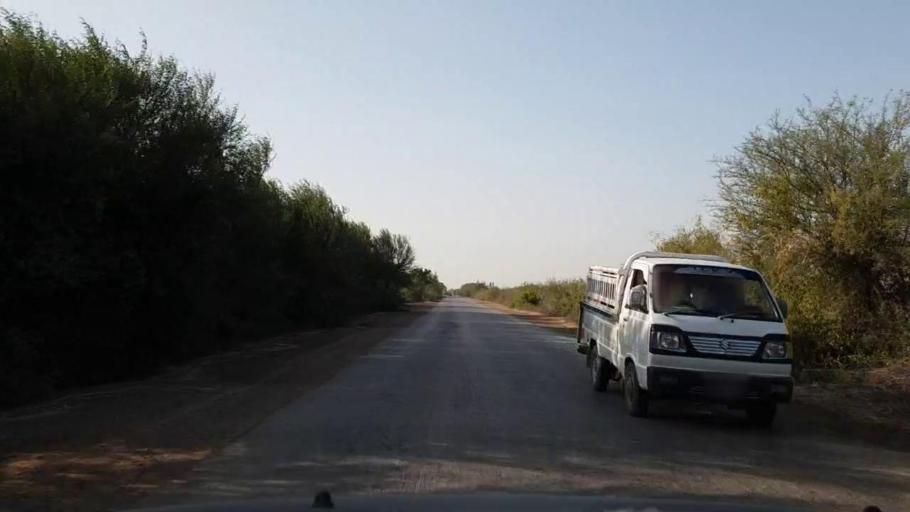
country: PK
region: Sindh
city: Tando Ghulam Ali
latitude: 25.1902
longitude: 68.8093
